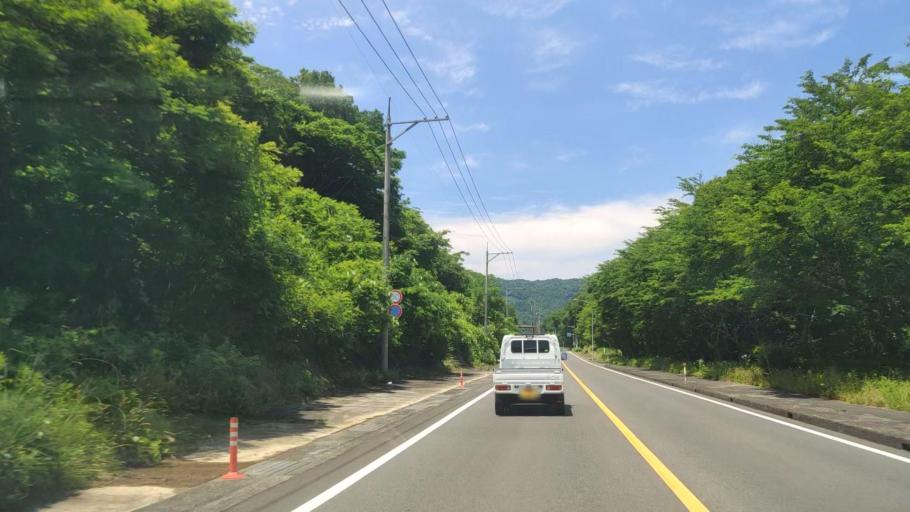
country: JP
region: Tottori
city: Tottori
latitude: 35.4022
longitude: 134.2599
